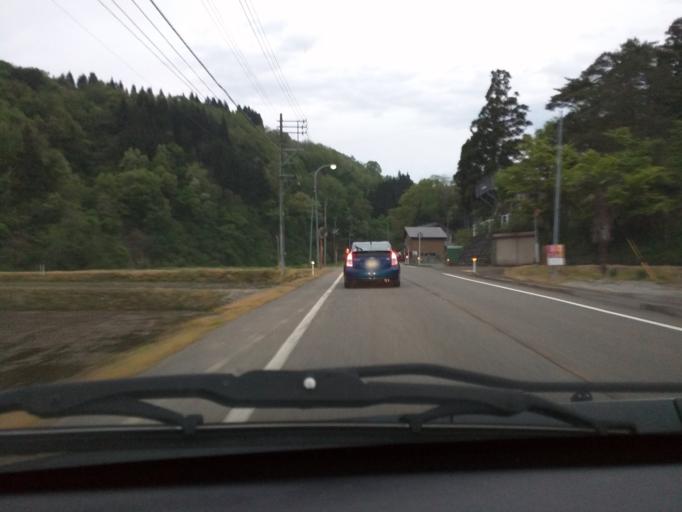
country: JP
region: Niigata
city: Ojiya
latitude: 37.3198
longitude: 138.7038
